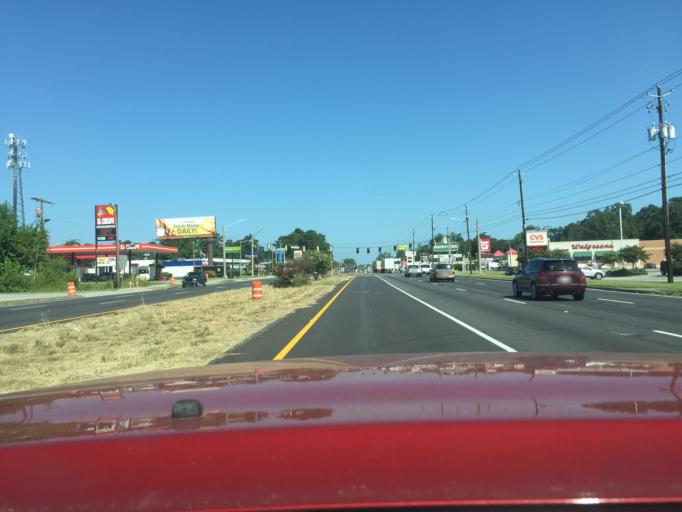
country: US
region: Georgia
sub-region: Chatham County
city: Garden City
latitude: 32.1023
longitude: -81.1475
